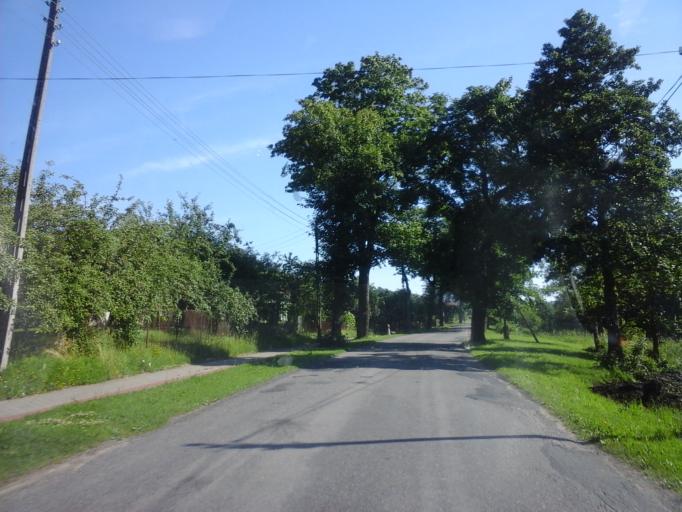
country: PL
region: West Pomeranian Voivodeship
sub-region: Powiat swidwinski
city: Polczyn-Zdroj
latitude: 53.6942
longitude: 16.0503
